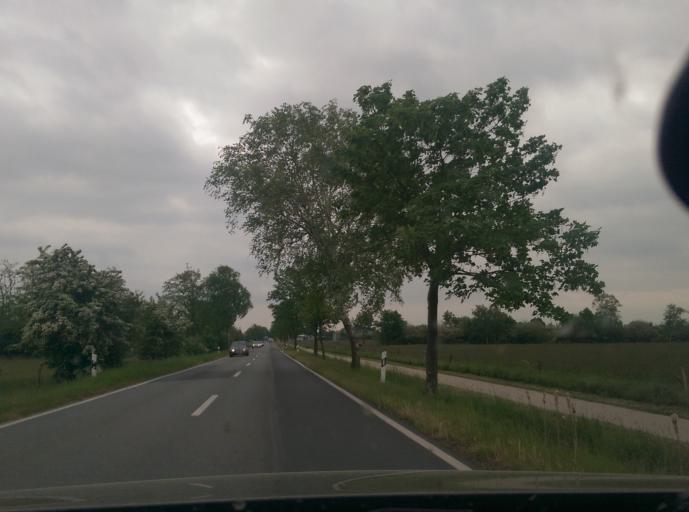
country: DE
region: Lower Saxony
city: Garbsen-Mitte
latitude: 52.4550
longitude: 9.6045
